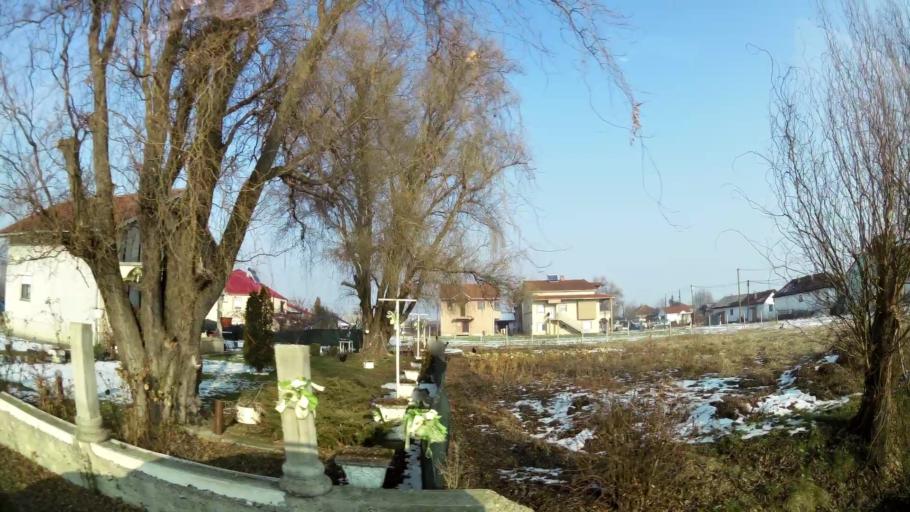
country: MK
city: Kadino
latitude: 41.9641
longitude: 21.5947
